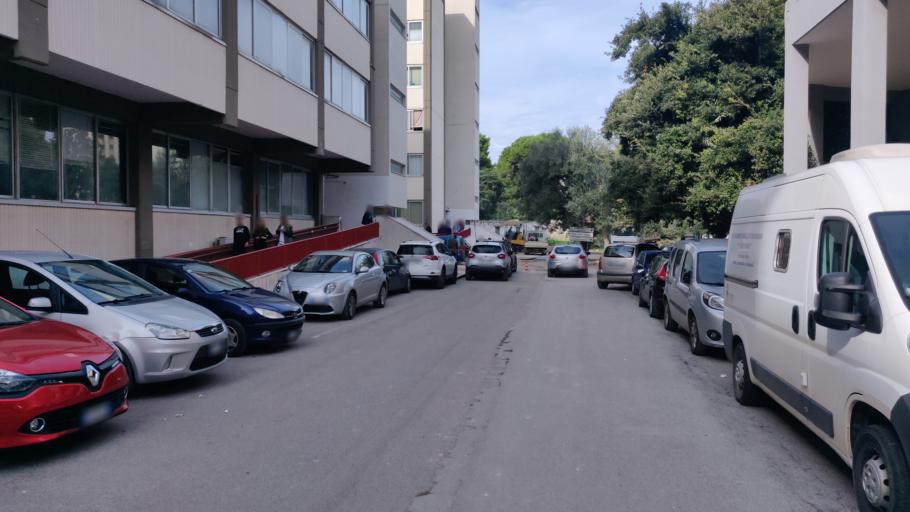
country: IT
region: Apulia
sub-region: Provincia di Bari
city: Bari
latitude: 41.1104
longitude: 16.8827
